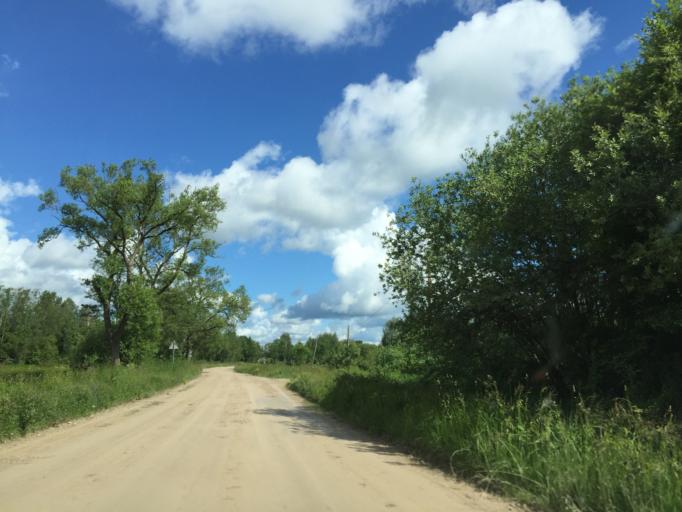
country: LV
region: Lecava
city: Iecava
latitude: 56.6154
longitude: 24.1886
